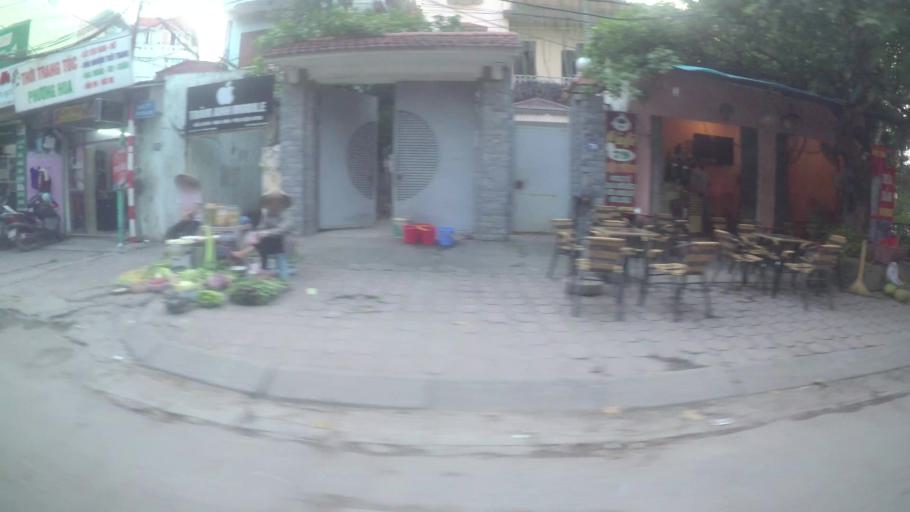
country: VN
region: Ha Noi
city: Cau Giay
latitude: 21.0482
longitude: 105.7900
